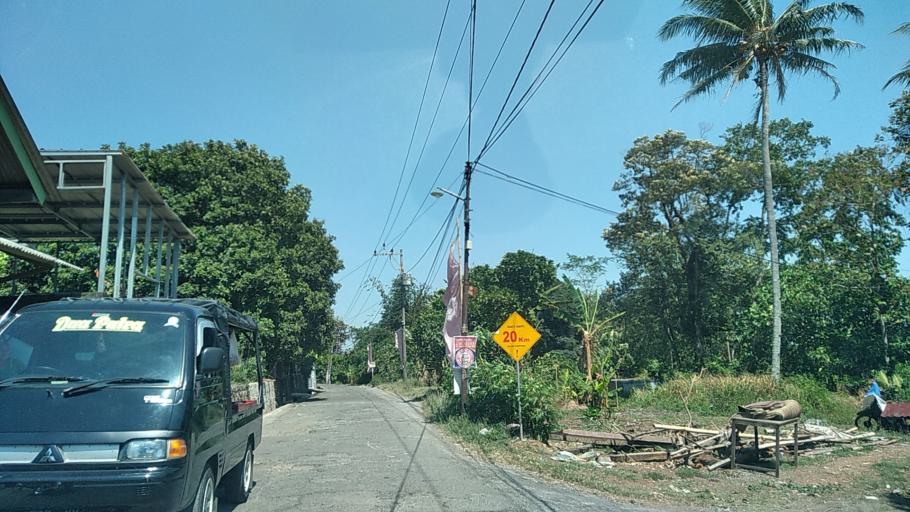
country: ID
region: Central Java
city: Ungaran
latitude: -7.0974
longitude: 110.4075
